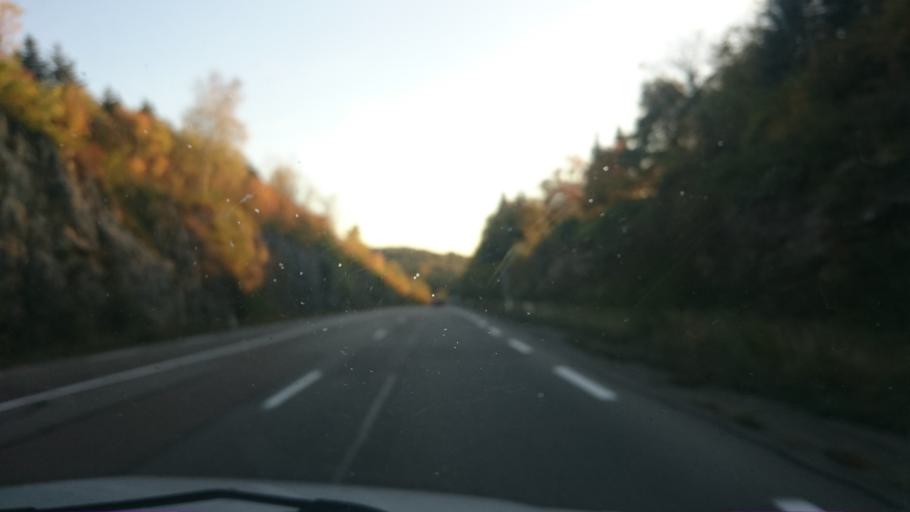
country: FR
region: Franche-Comte
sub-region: Departement du Jura
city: Mouchard
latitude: 46.9716
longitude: 5.8021
